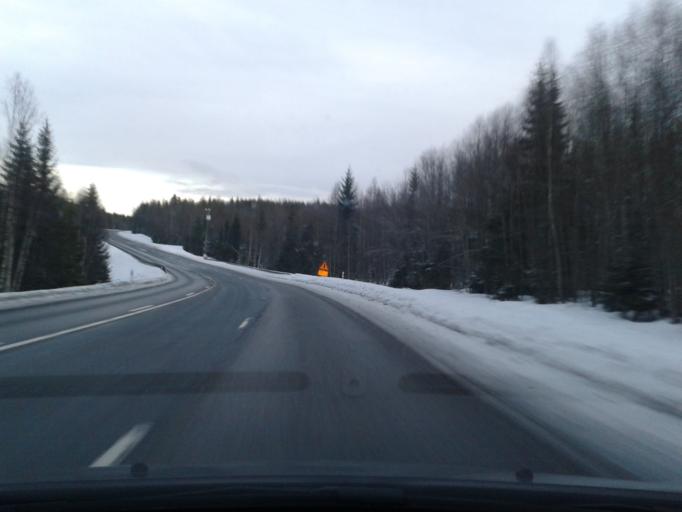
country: SE
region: Vaesternorrland
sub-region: Solleftea Kommun
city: Solleftea
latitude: 63.1302
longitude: 17.4708
